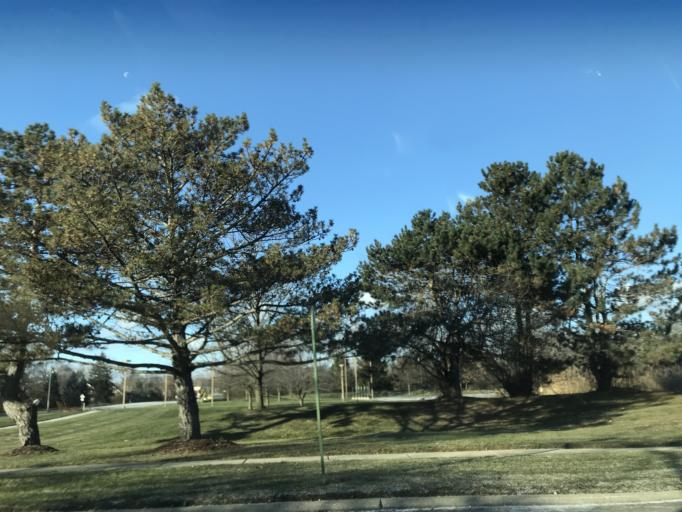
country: US
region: Michigan
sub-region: Oakland County
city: Troy
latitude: 42.5772
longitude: -83.1624
